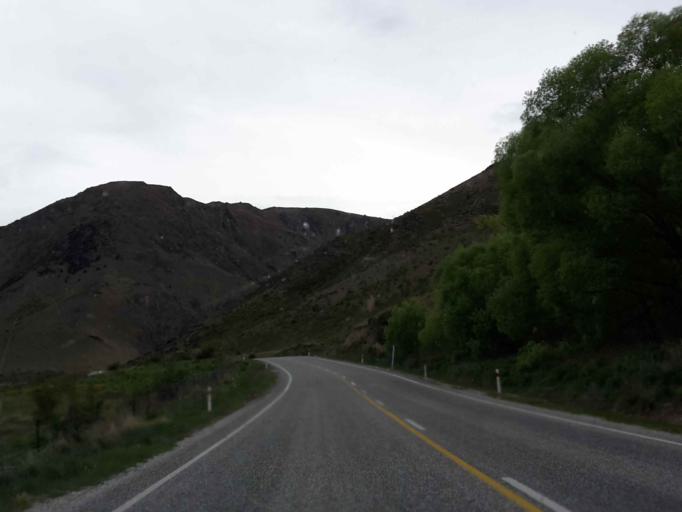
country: NZ
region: Otago
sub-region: Queenstown-Lakes District
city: Wanaka
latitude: -44.6108
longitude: 169.5326
